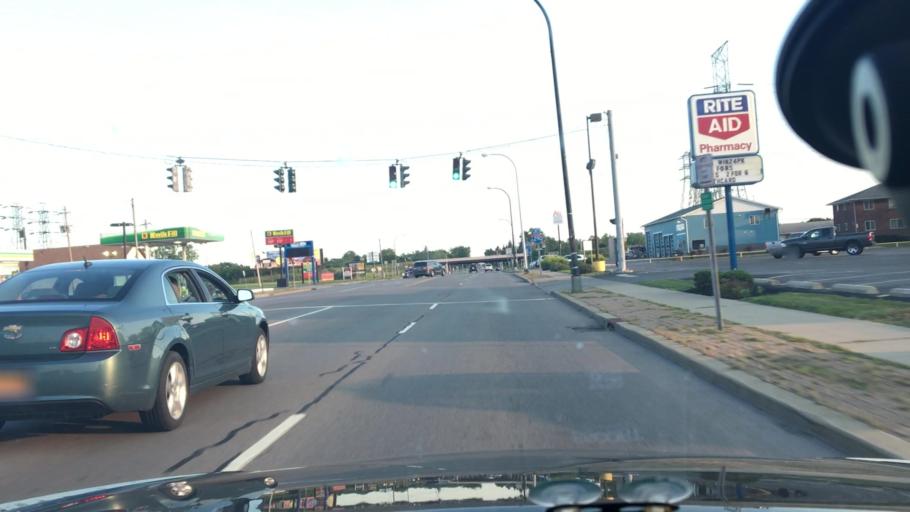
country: US
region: New York
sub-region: Erie County
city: Tonawanda
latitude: 42.9994
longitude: -78.8751
